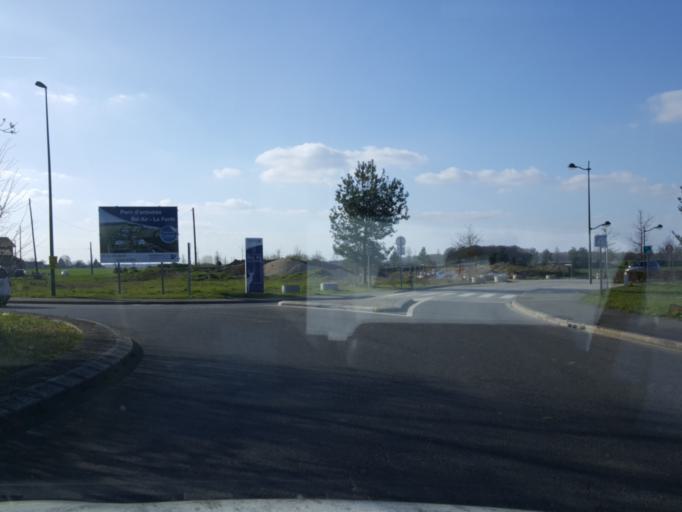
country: FR
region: Ile-de-France
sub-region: Departement des Yvelines
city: Rambouillet
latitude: 48.6220
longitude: 1.8157
